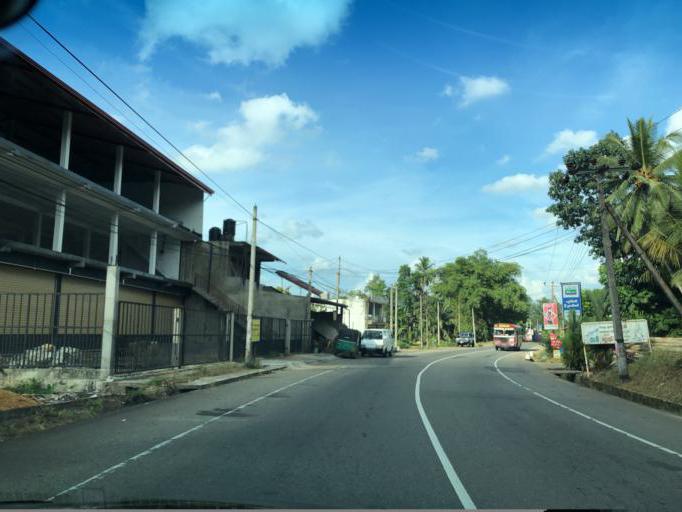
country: LK
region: Western
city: Horawala Junction
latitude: 6.5248
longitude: 80.0870
